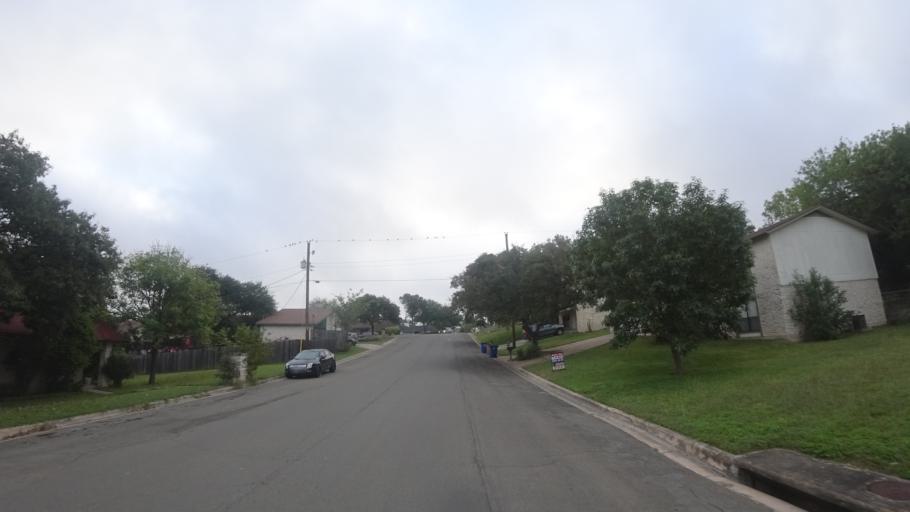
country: US
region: Texas
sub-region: Travis County
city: Wells Branch
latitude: 30.3696
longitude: -97.6667
